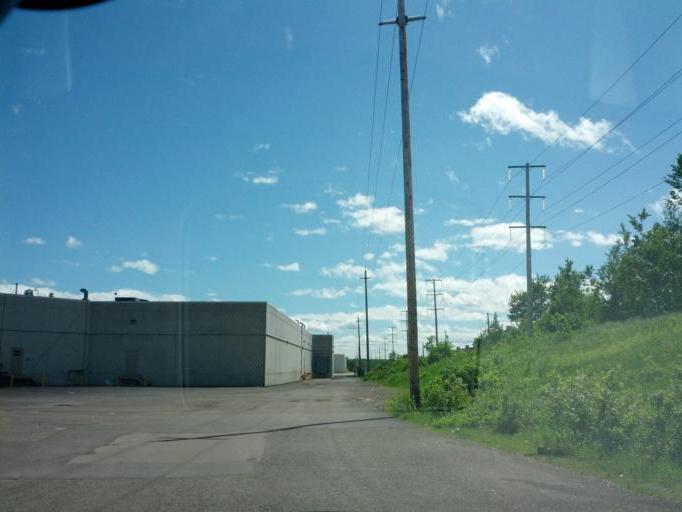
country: CA
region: New Brunswick
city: Moncton
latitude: 46.1186
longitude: -64.8335
